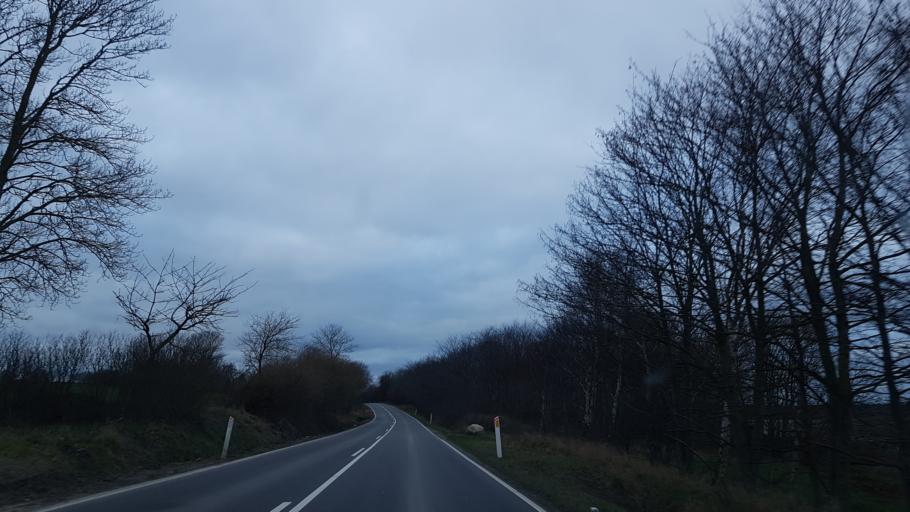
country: DK
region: Zealand
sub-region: Odsherred Kommune
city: Hojby
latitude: 55.9325
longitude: 11.5975
